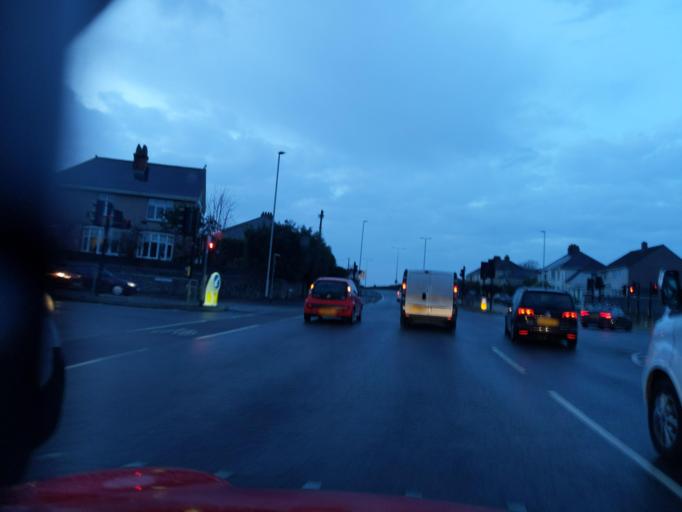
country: GB
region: England
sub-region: Plymouth
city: Plymstock
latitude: 50.3612
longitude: -4.0659
